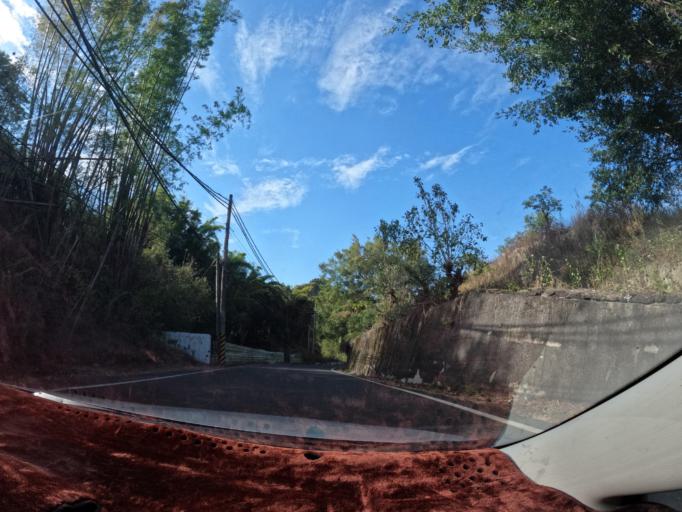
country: TW
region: Taiwan
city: Yujing
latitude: 23.0232
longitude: 120.3956
